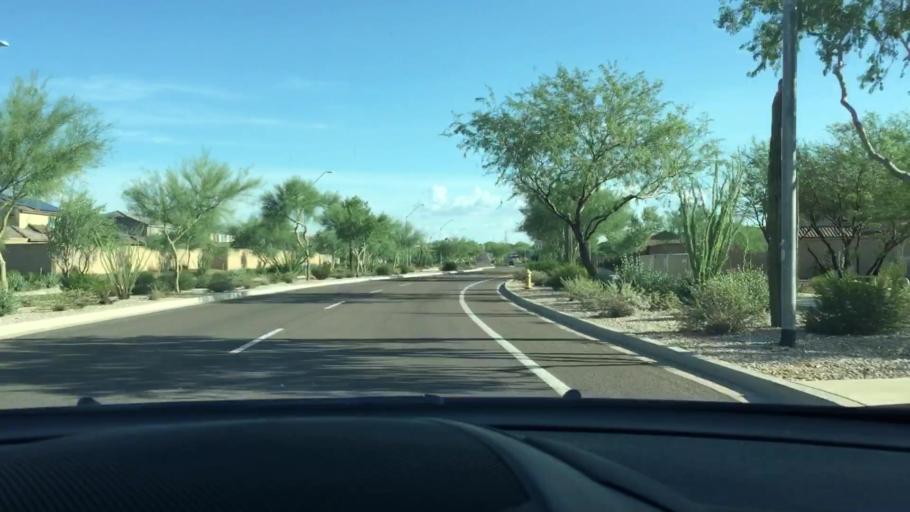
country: US
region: Arizona
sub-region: Maricopa County
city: Sun City West
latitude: 33.7205
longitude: -112.2852
